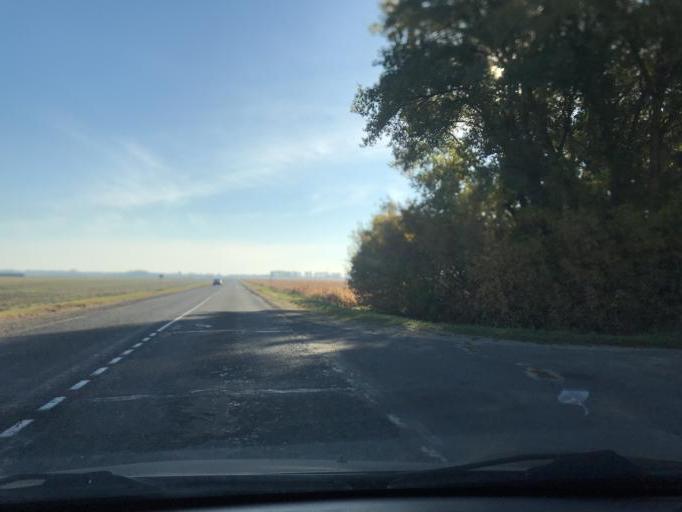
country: BY
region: Gomel
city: Brahin
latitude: 51.7820
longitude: 30.2215
